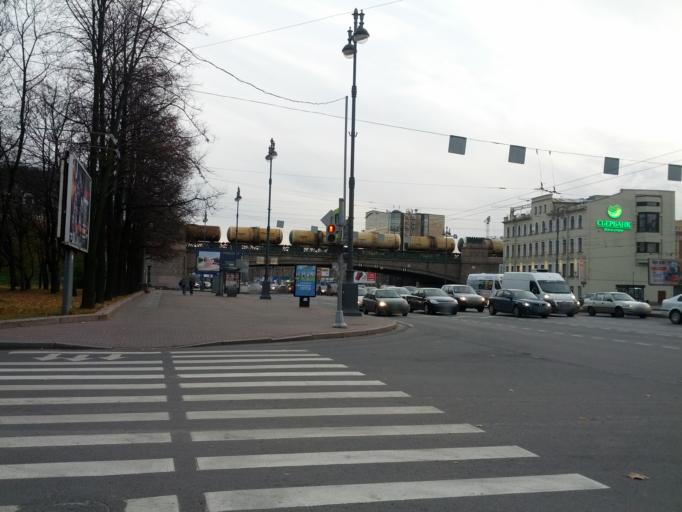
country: RU
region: St.-Petersburg
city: Admiralteisky
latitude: 59.8841
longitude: 30.3206
